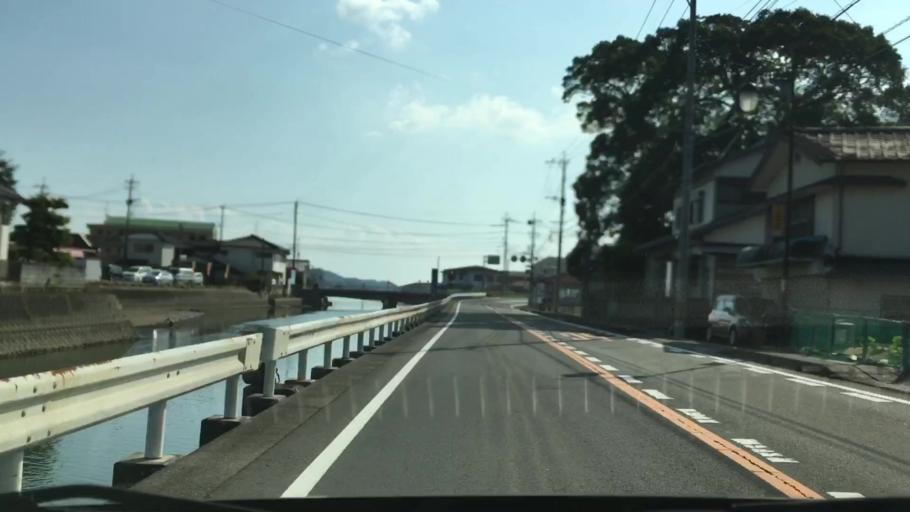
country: JP
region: Nagasaki
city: Togitsu
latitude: 32.9513
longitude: 129.7849
